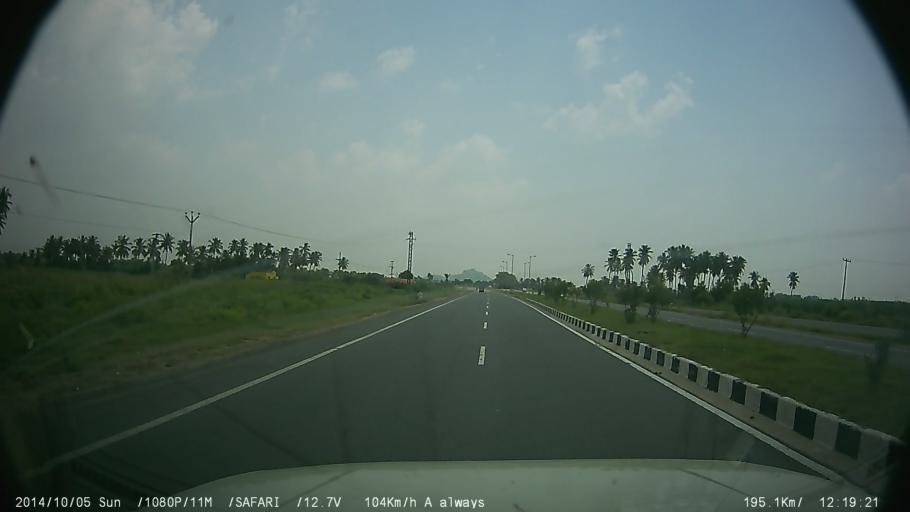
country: IN
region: Tamil Nadu
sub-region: Villupuram
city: Kallakkurichchi
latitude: 11.7347
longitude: 79.0357
